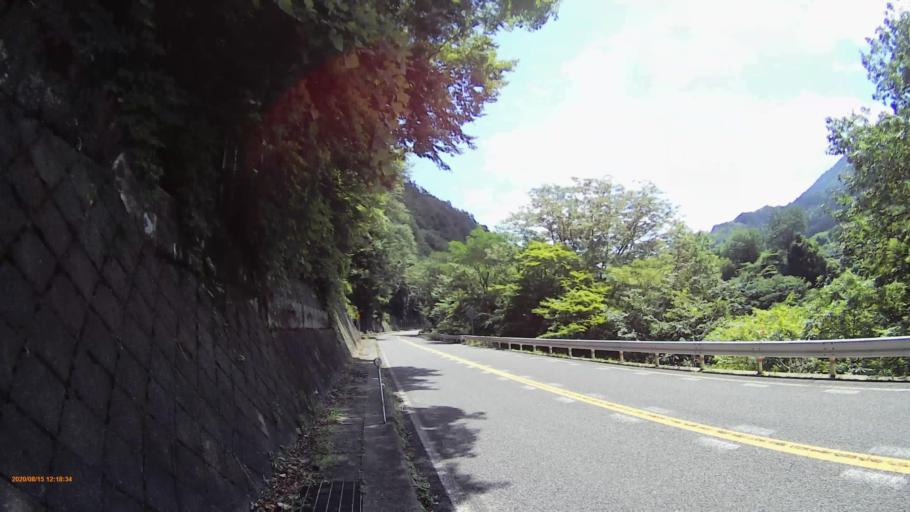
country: JP
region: Nagano
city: Ina
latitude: 35.8097
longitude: 137.6863
